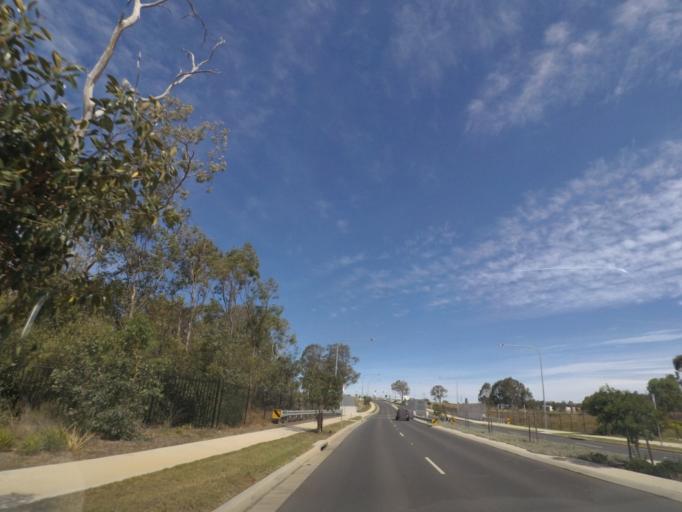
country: AU
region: New South Wales
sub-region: Camden
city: Narellan Vale
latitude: -34.0292
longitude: 150.7869
